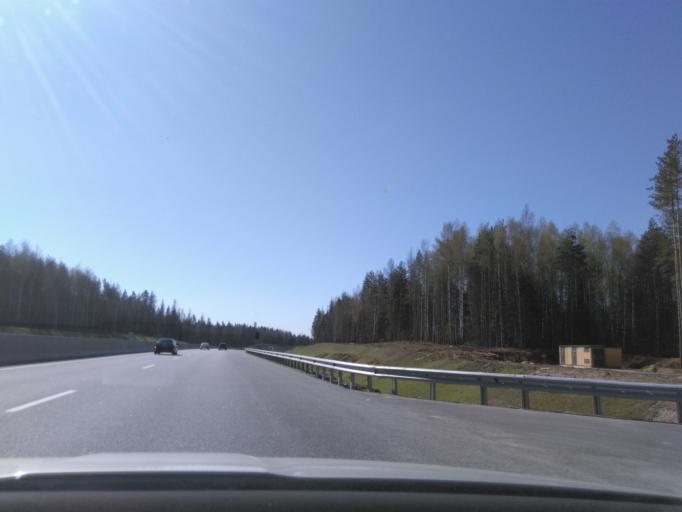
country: RU
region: Moskovskaya
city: Mendeleyevo
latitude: 56.0498
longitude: 37.2606
